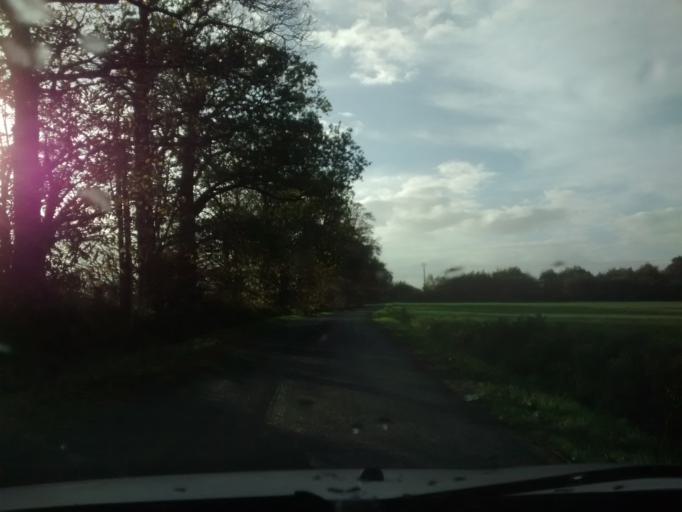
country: FR
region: Brittany
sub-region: Departement d'Ille-et-Vilaine
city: Acigne
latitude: 48.1212
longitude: -1.5618
